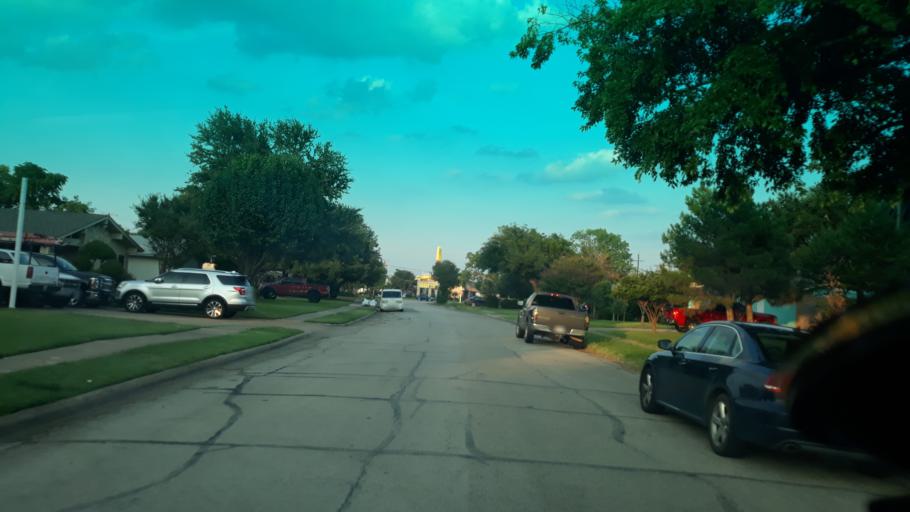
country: US
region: Texas
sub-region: Dallas County
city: Irving
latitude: 32.8395
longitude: -96.9784
